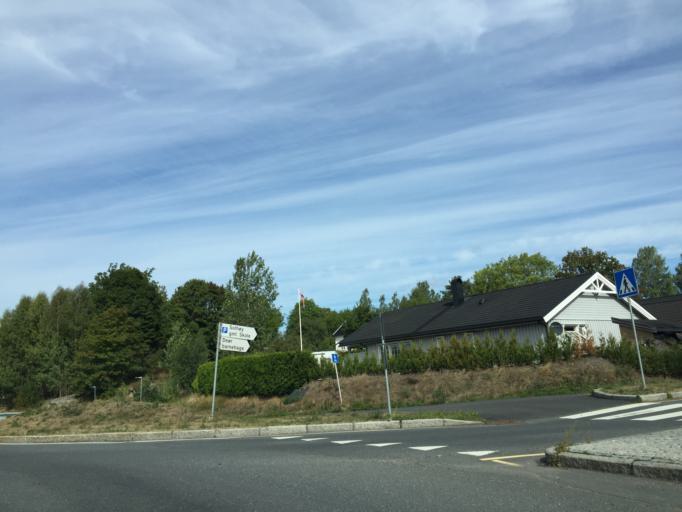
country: NO
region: Ostfold
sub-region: Moss
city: Moss
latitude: 59.5193
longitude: 10.7027
